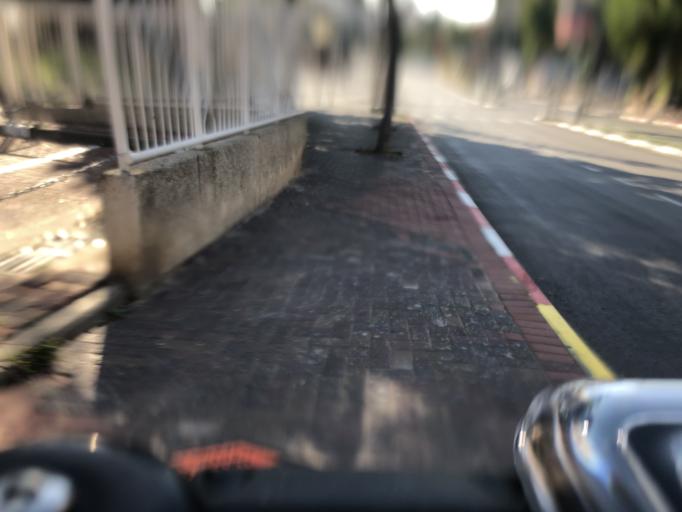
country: IL
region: Tel Aviv
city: Giv`atayim
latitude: 32.0679
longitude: 34.8086
